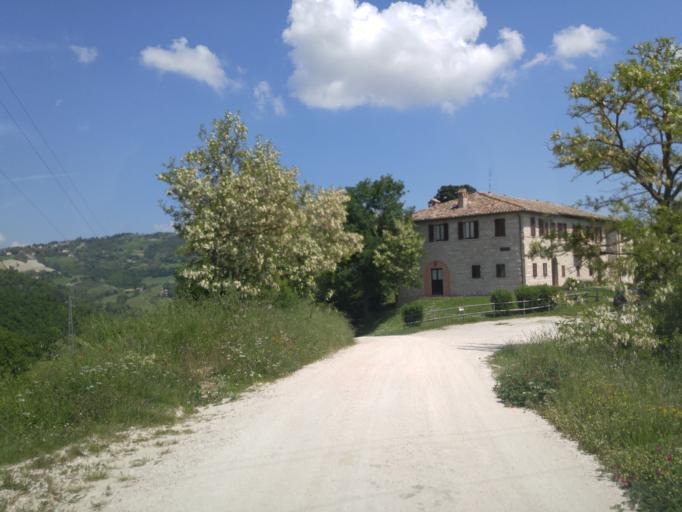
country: IT
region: The Marches
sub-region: Provincia di Pesaro e Urbino
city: Fermignano
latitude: 43.7019
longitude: 12.6525
